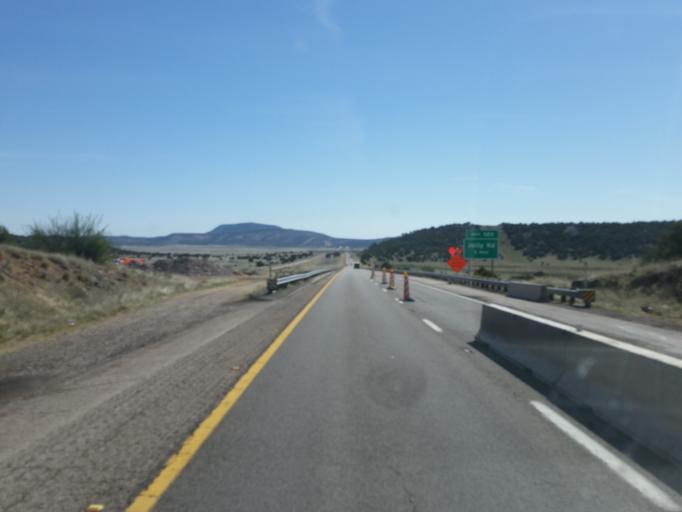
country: US
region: Arizona
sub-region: Mohave County
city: Peach Springs
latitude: 35.2421
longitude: -113.1968
